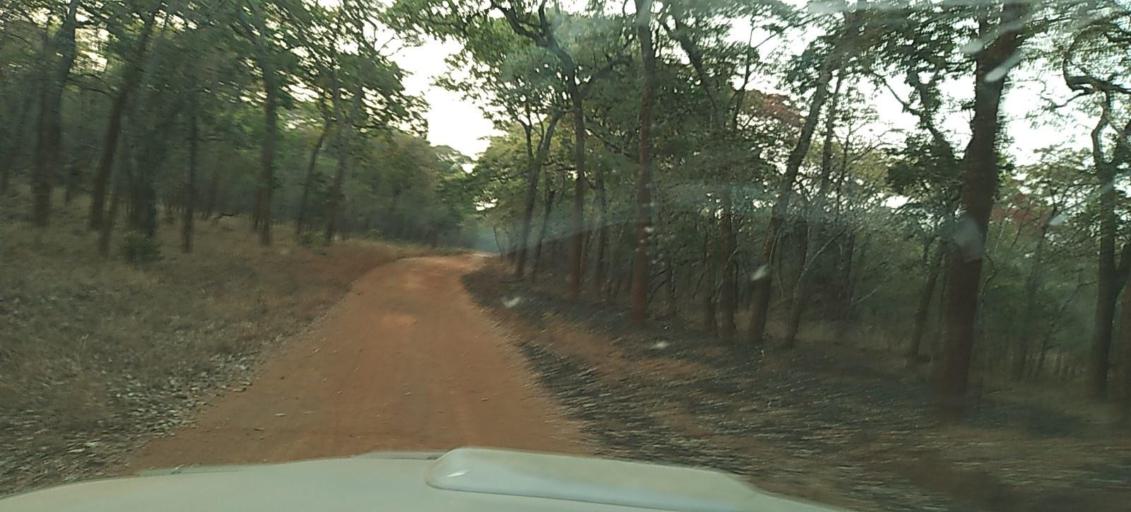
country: ZM
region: North-Western
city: Kasempa
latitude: -13.0983
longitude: 26.4029
